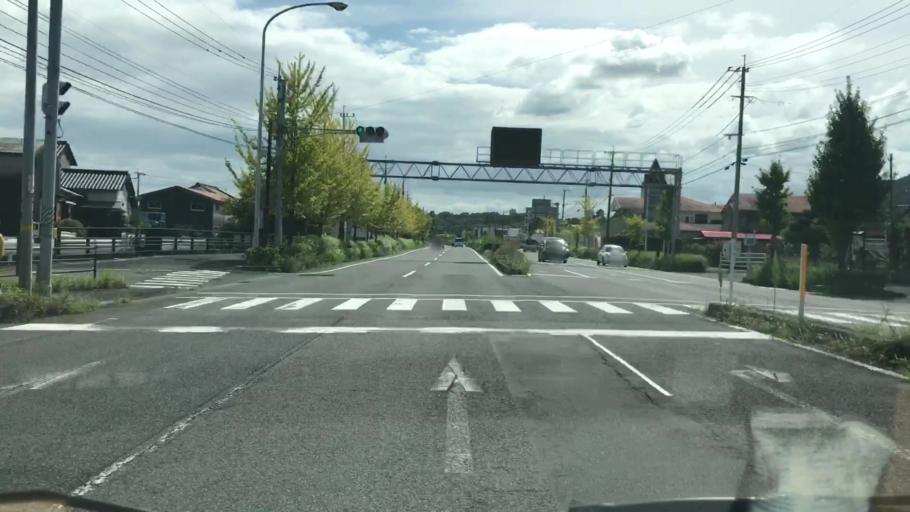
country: JP
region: Saga Prefecture
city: Saga-shi
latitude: 33.2405
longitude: 130.1845
